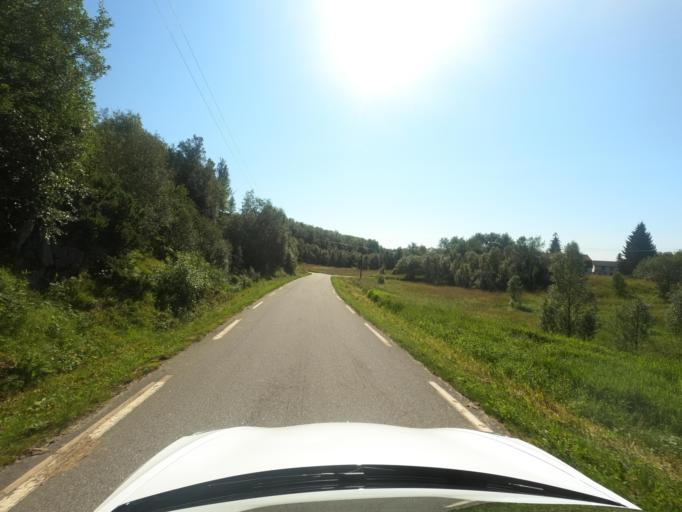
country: NO
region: Nordland
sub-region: Hadsel
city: Stokmarknes
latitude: 68.3038
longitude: 15.0944
